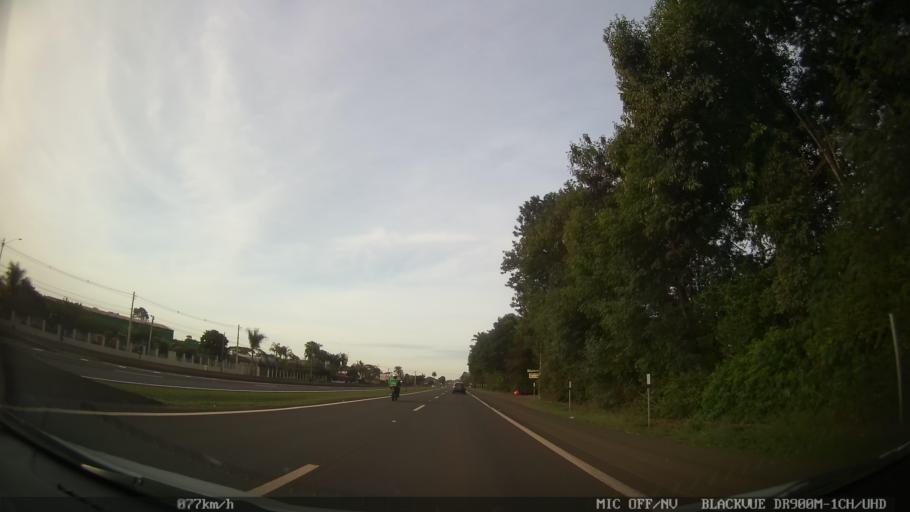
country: BR
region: Sao Paulo
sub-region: Iracemapolis
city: Iracemapolis
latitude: -22.5971
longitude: -47.4694
